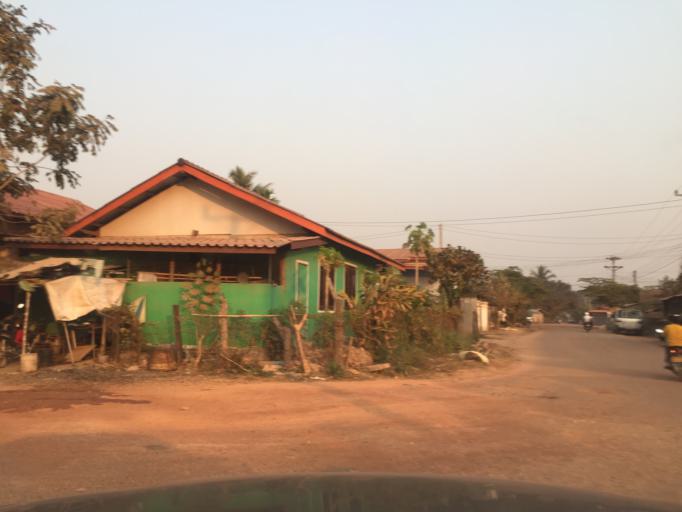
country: LA
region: Vientiane
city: Vientiane
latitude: 18.0609
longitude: 102.5270
